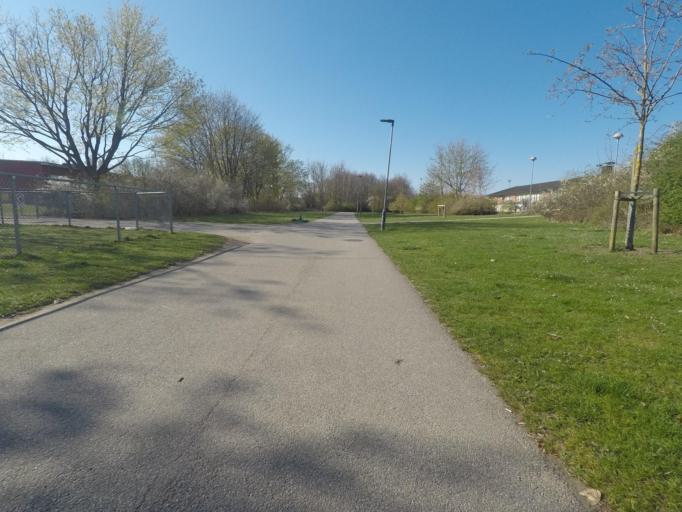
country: SE
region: Skane
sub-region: Malmo
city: Tygelsjo
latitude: 55.5571
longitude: 13.0125
